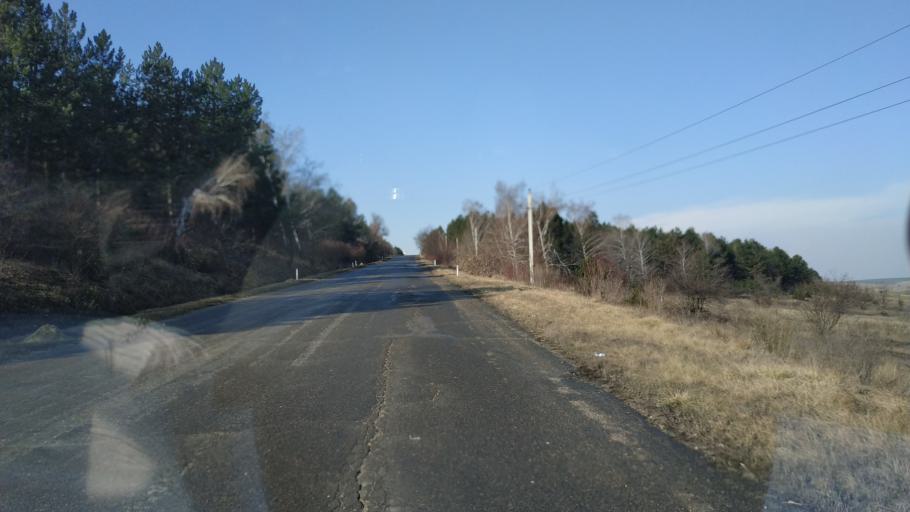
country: MD
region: Chisinau
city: Singera
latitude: 46.6973
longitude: 29.0649
